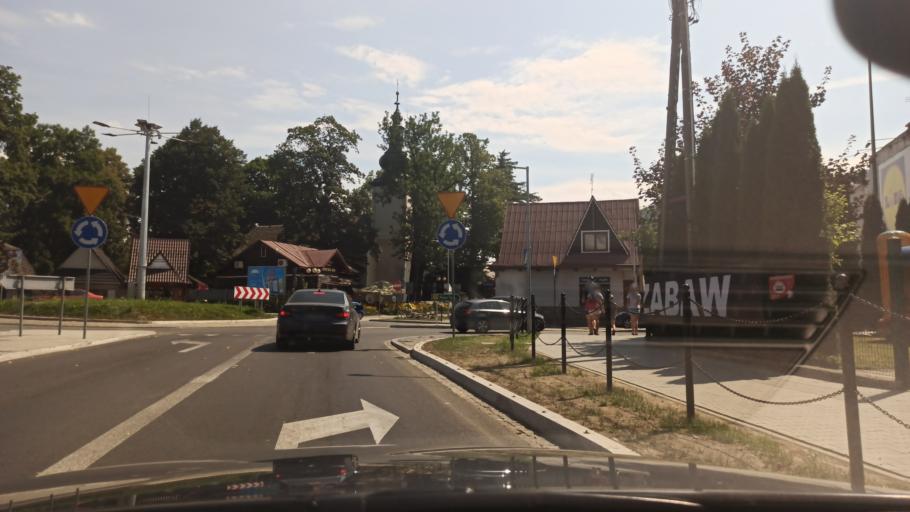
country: PL
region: Lesser Poland Voivodeship
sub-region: Powiat nowotarski
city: Kroscienko nad Dunajcem
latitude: 49.4416
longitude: 20.4285
